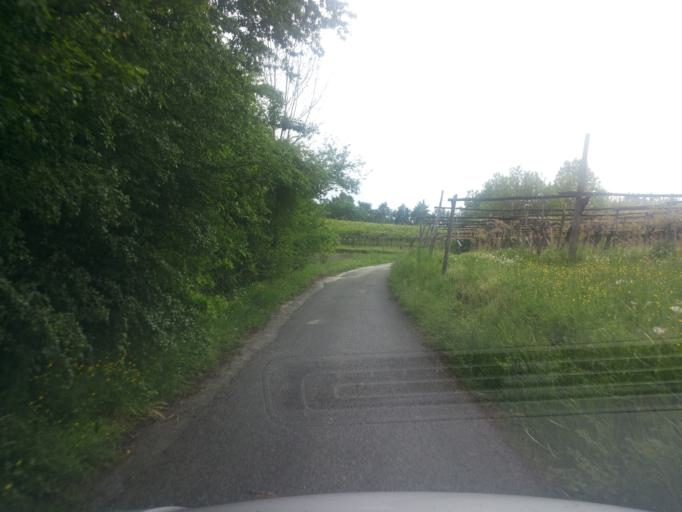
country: IT
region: Piedmont
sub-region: Provincia di Torino
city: Cossano Canavese
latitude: 45.3926
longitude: 8.0110
